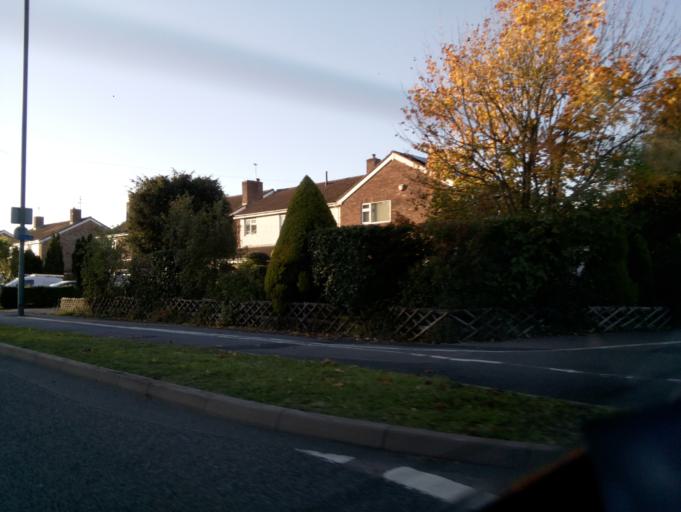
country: GB
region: England
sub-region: Gloucestershire
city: Tewkesbury
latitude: 51.9970
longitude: -2.1311
